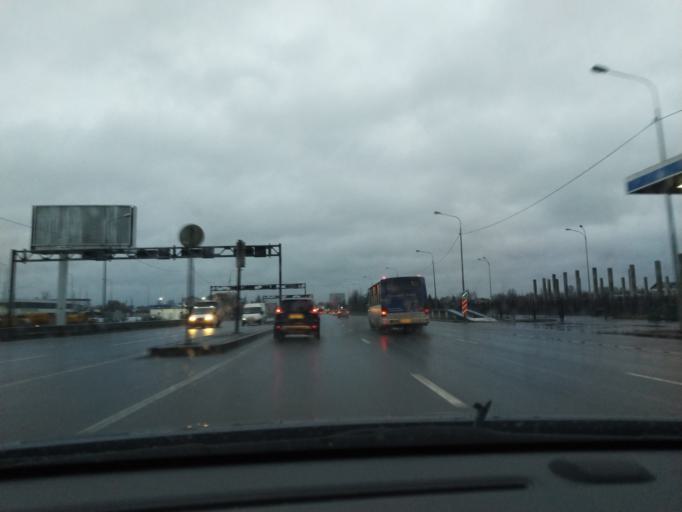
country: RU
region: St.-Petersburg
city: Uritsk
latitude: 59.8090
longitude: 30.1676
